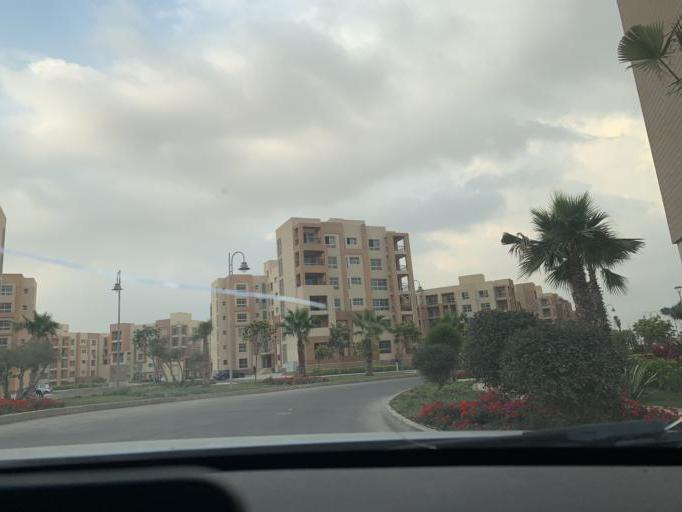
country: EG
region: Muhafazat al Qalyubiyah
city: Al Khankah
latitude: 30.1023
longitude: 31.6503
